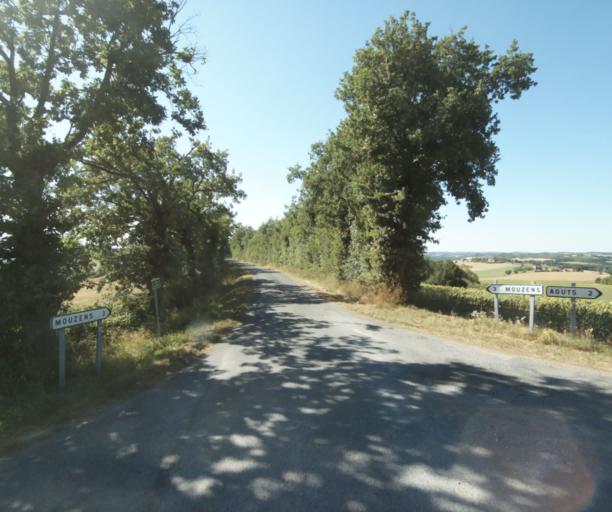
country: FR
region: Midi-Pyrenees
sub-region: Departement de la Haute-Garonne
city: Saint-Felix-Lauragais
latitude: 43.5205
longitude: 1.9137
